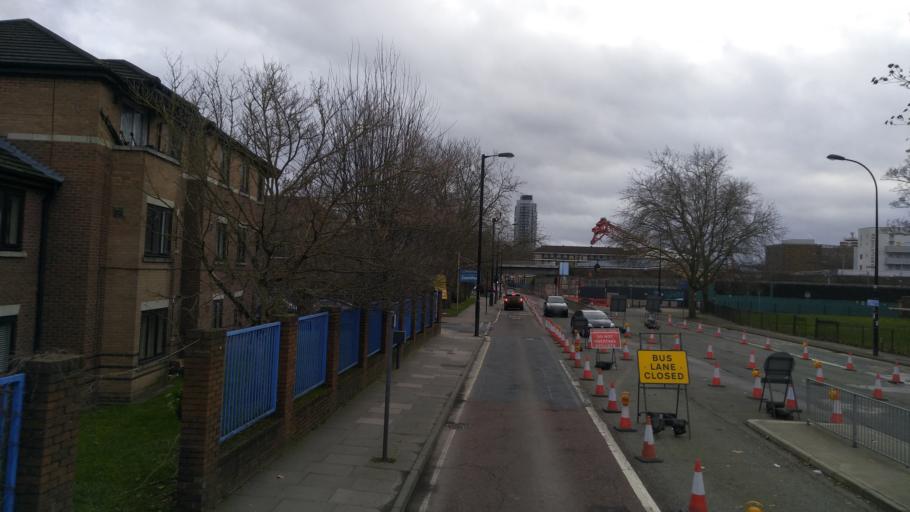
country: GB
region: England
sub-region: Greater London
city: Poplar
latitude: 51.4801
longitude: -0.0229
